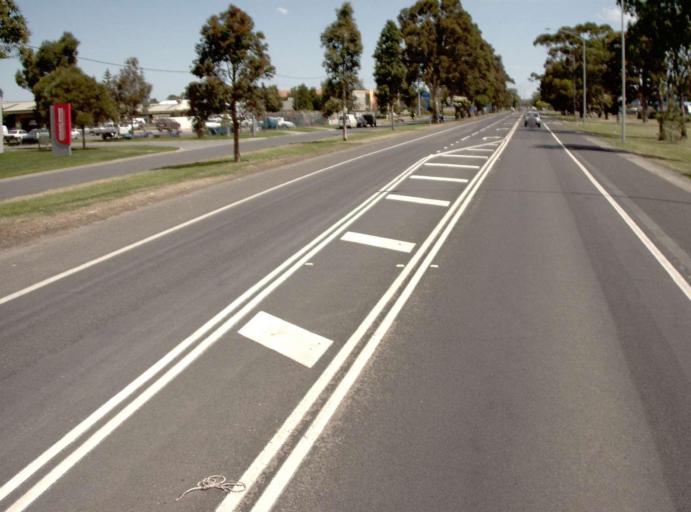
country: AU
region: Victoria
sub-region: Wellington
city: Sale
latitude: -38.0887
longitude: 147.0698
